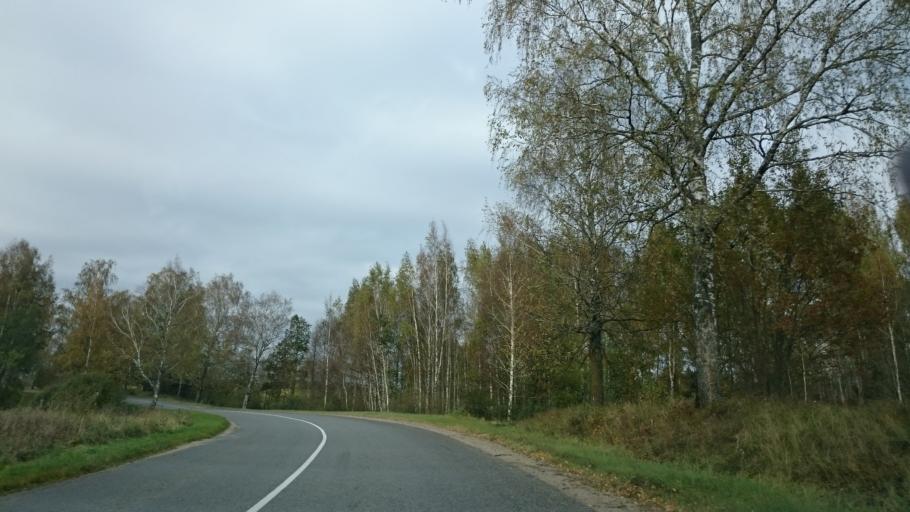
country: LV
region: Amatas Novads
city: Drabesi
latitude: 57.2762
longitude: 25.2701
